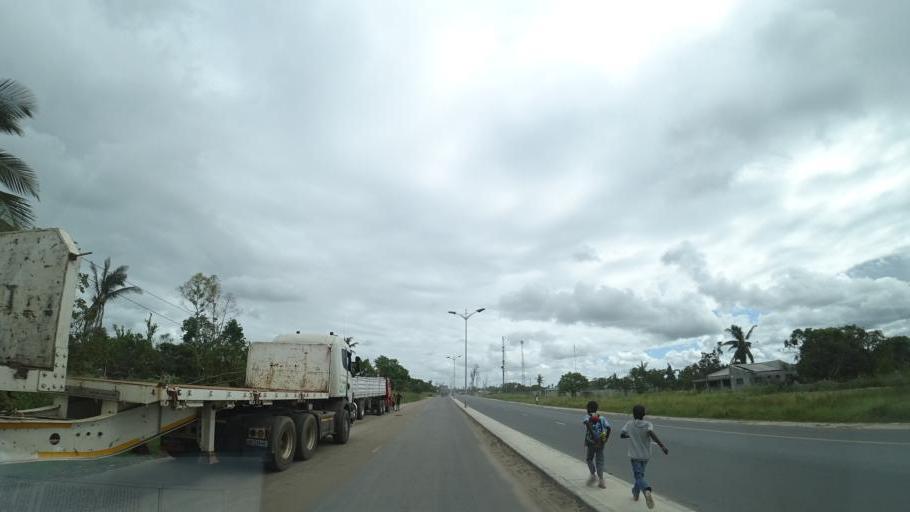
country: MZ
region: Sofala
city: Dondo
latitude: -19.6963
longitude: 34.7820
